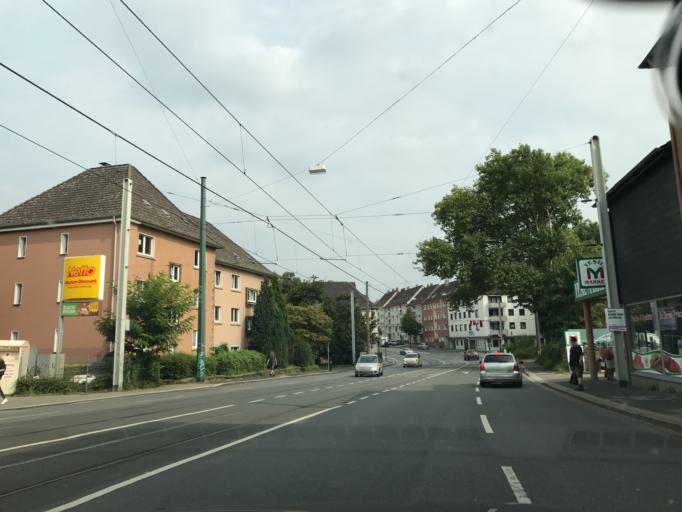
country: DE
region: North Rhine-Westphalia
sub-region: Regierungsbezirk Dusseldorf
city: Essen
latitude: 51.4614
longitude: 6.9656
